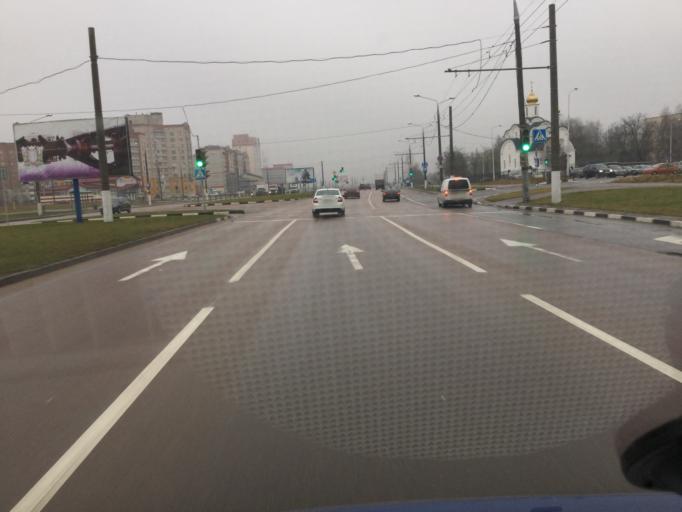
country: BY
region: Vitebsk
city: Vitebsk
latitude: 55.1609
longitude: 30.2248
